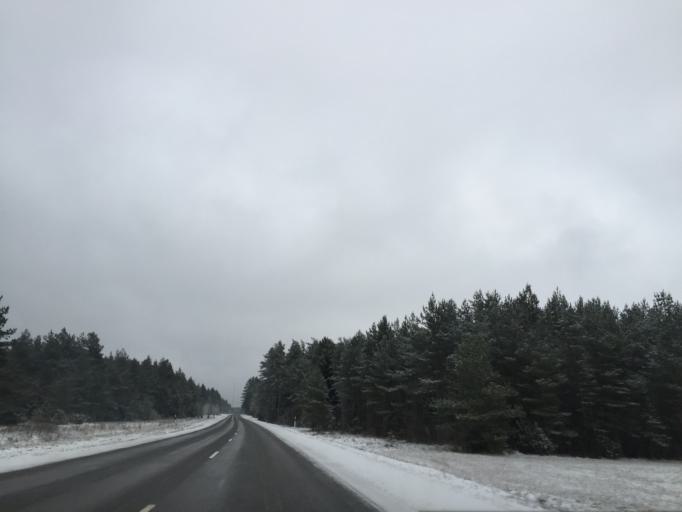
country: EE
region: Laeaene
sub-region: Lihula vald
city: Lihula
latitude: 58.6105
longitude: 23.9317
